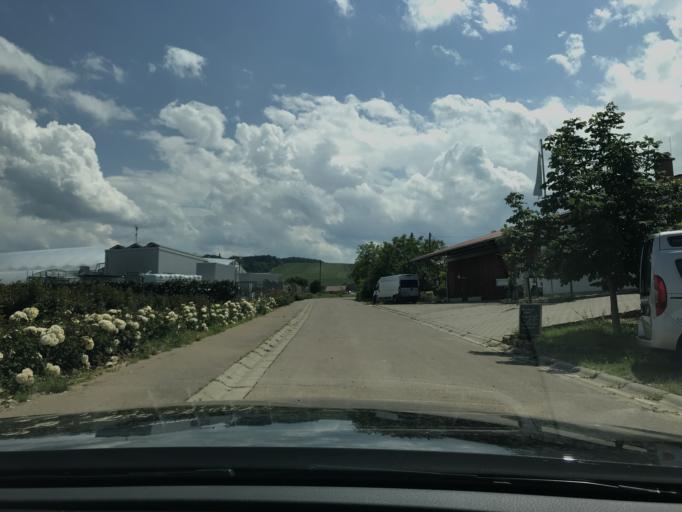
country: DE
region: Baden-Wuerttemberg
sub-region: Regierungsbezirk Stuttgart
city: Weinstadt-Endersbach
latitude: 48.8040
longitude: 9.3677
